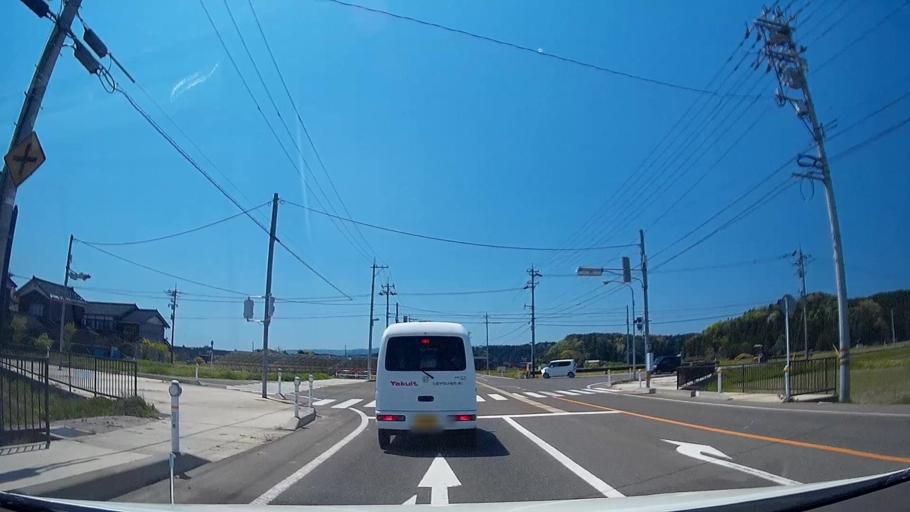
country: JP
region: Ishikawa
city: Nanao
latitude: 37.4499
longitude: 137.2898
